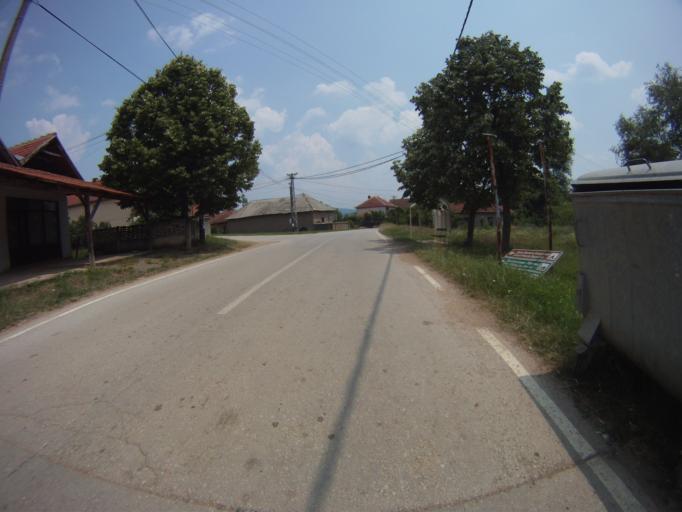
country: RS
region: Central Serbia
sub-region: Nisavski Okrug
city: Gadzin Han
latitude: 43.2076
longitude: 21.9878
